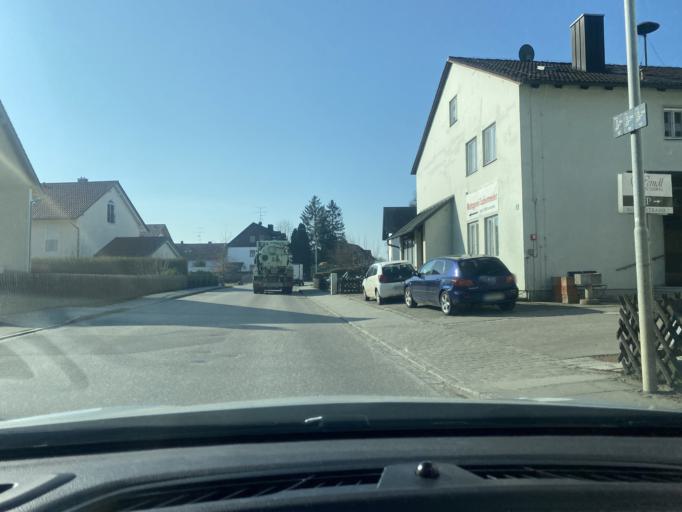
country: DE
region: Bavaria
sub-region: Upper Bavaria
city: Oberding
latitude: 48.3038
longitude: 11.8475
